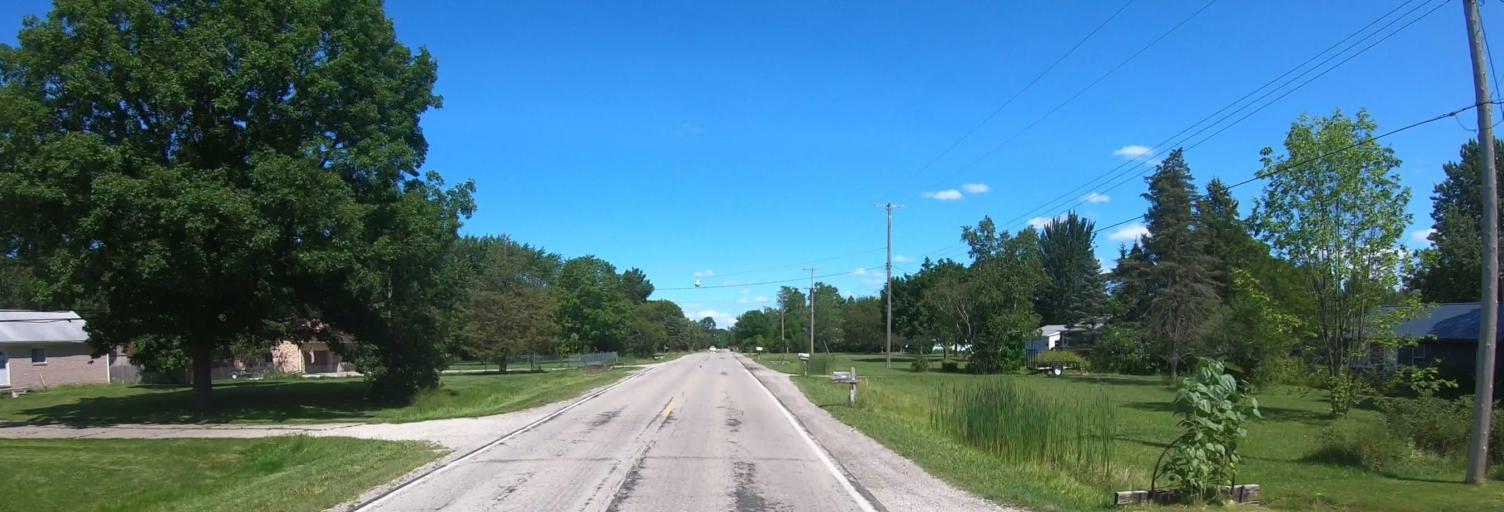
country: US
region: Michigan
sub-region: Genesee County
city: Flushing
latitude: 43.0786
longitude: -83.7807
